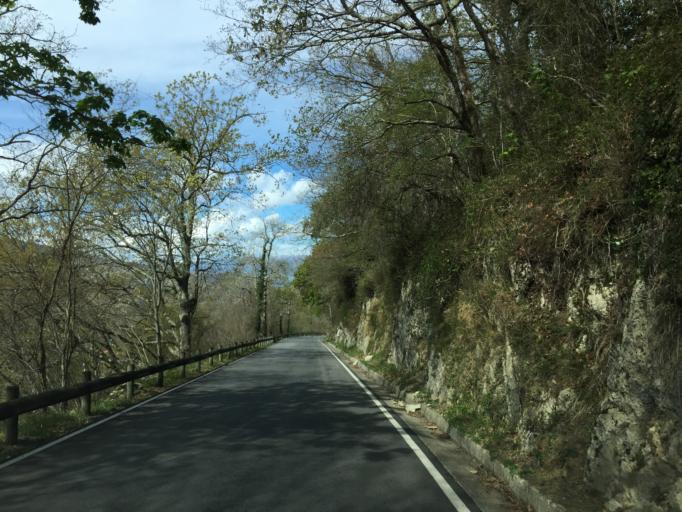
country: ES
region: Asturias
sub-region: Province of Asturias
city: Amieva
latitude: 43.3042
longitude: -5.0425
